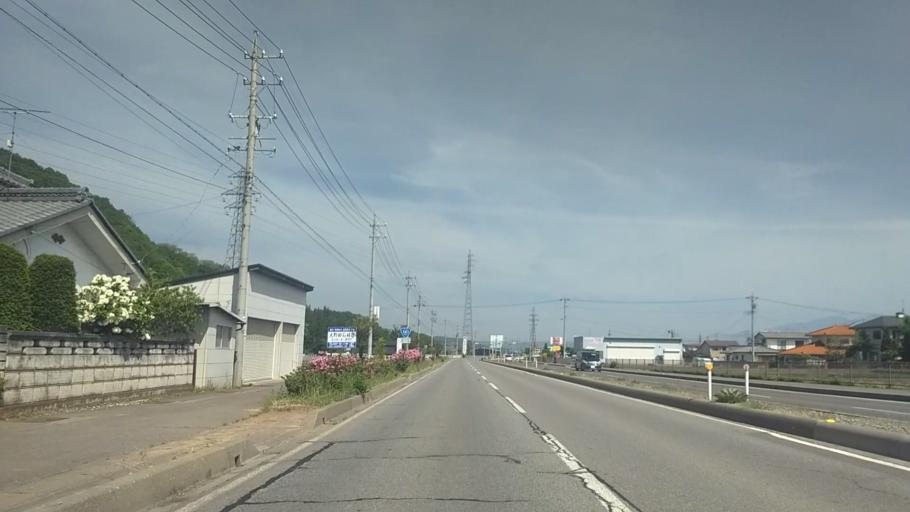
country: JP
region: Nagano
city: Saku
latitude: 36.1989
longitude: 138.4723
